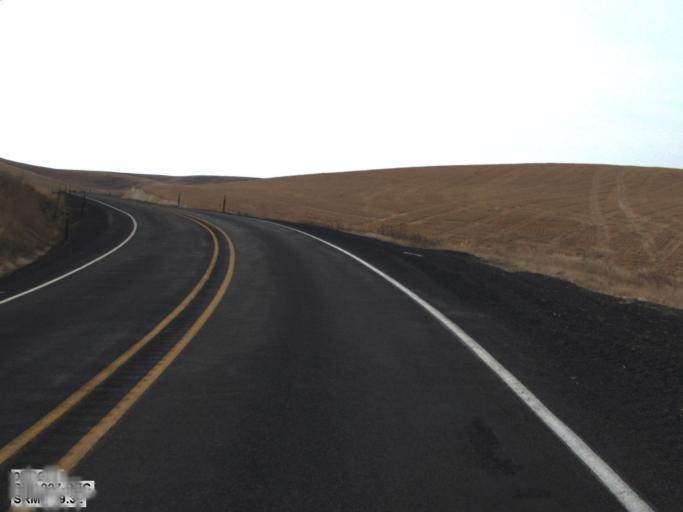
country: US
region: Idaho
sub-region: Latah County
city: Moscow
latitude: 46.9602
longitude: -117.0912
